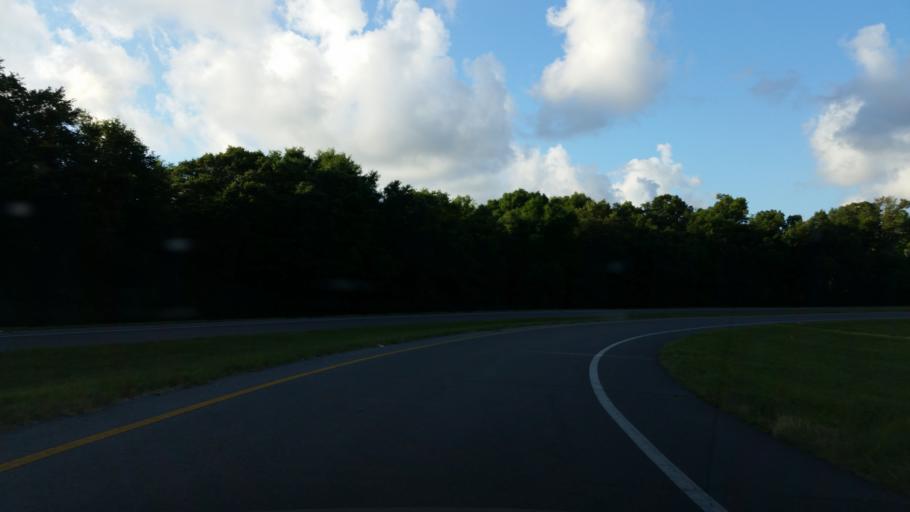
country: US
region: Florida
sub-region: Escambia County
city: West Pensacola
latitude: 30.4311
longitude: -87.2705
